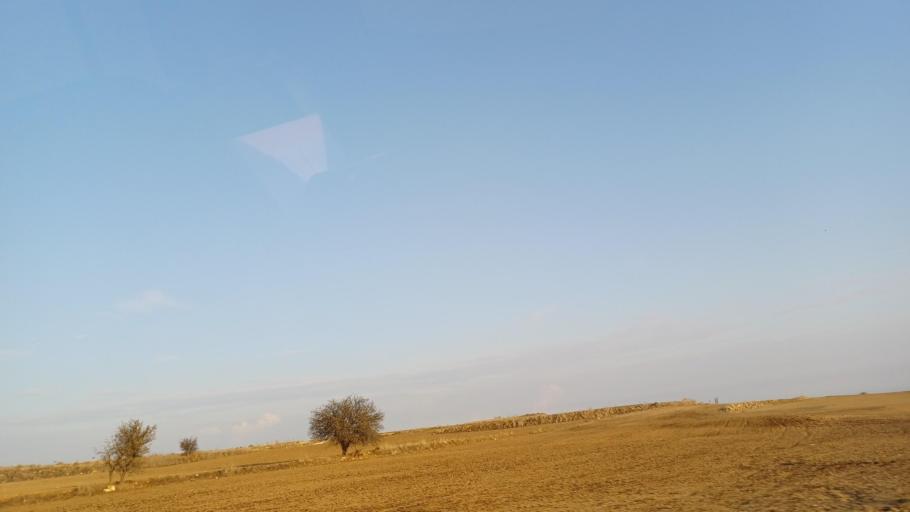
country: CY
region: Larnaka
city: Athienou
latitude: 35.0235
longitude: 33.5493
